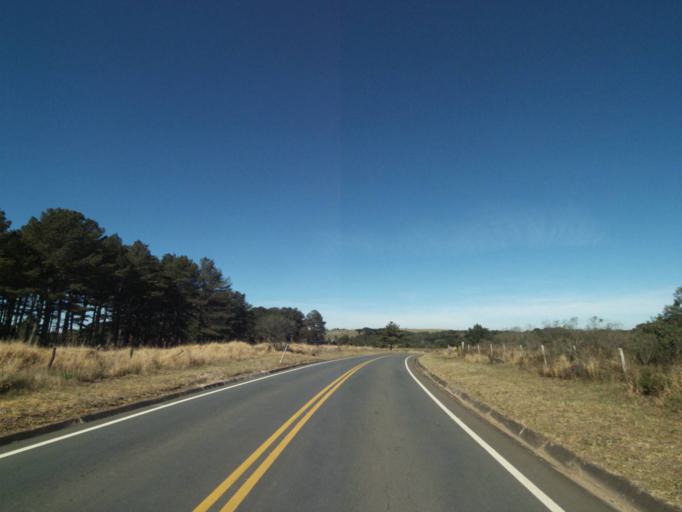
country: BR
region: Parana
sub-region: Castro
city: Castro
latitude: -24.7237
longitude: -50.1854
